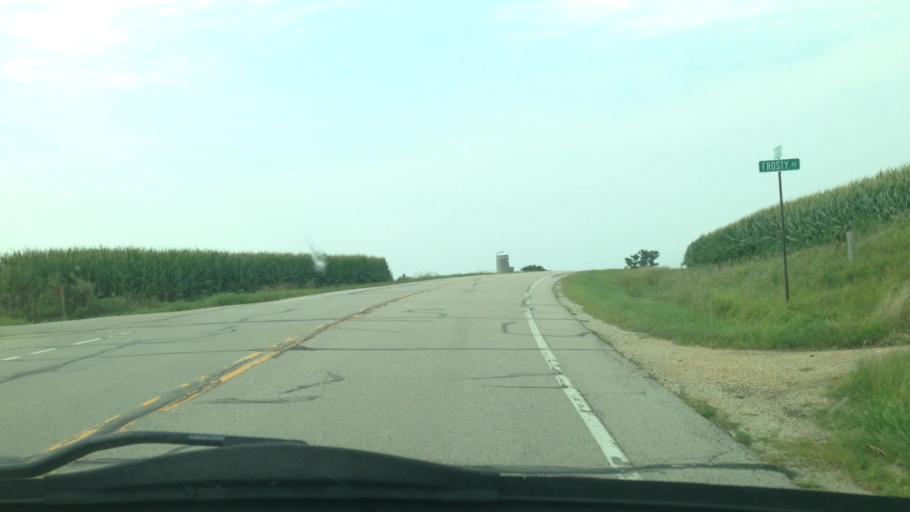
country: US
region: Minnesota
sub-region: Fillmore County
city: Preston
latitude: 43.7563
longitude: -91.9645
